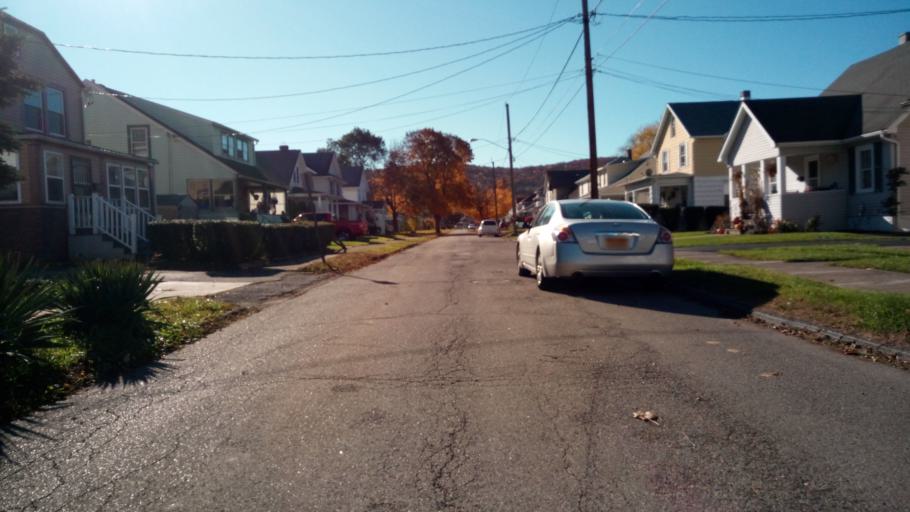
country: US
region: New York
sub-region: Chemung County
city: Southport
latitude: 42.0684
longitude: -76.8092
